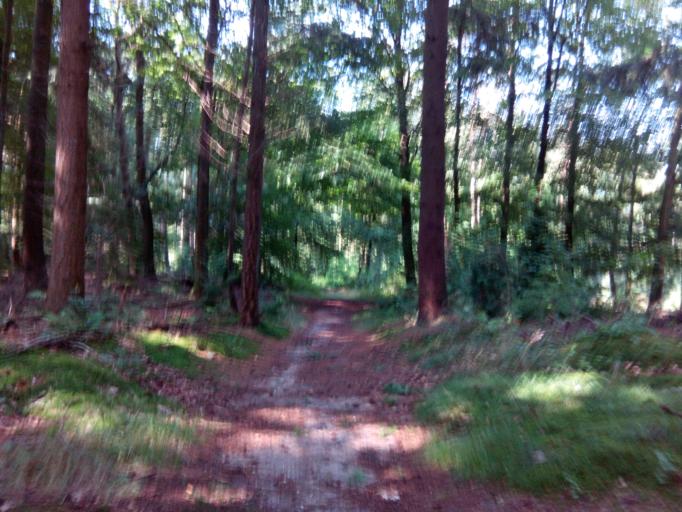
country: NL
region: Utrecht
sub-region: Gemeente Utrechtse Heuvelrug
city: Doorn
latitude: 52.0459
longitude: 5.3232
